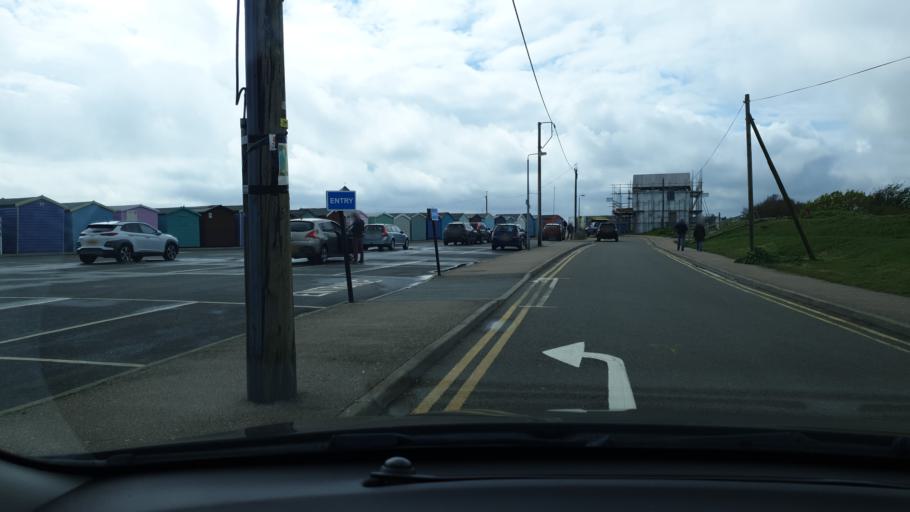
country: GB
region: England
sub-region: Essex
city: Brightlingsea
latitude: 51.8063
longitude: 1.0130
